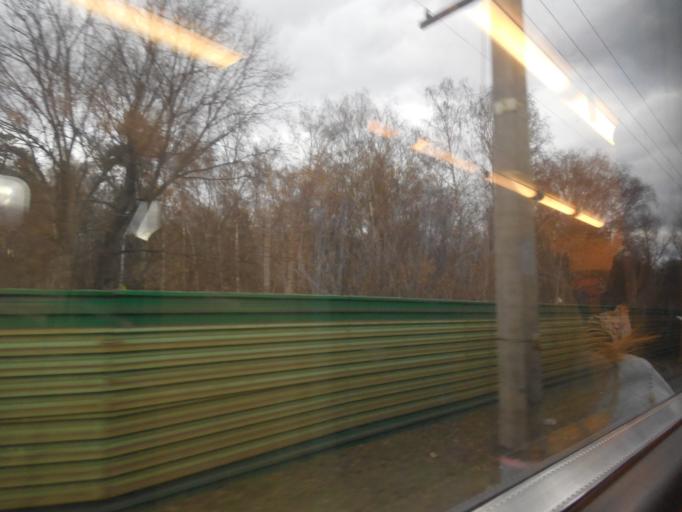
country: RU
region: Moskovskaya
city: Tomilino
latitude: 55.6559
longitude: 37.9532
